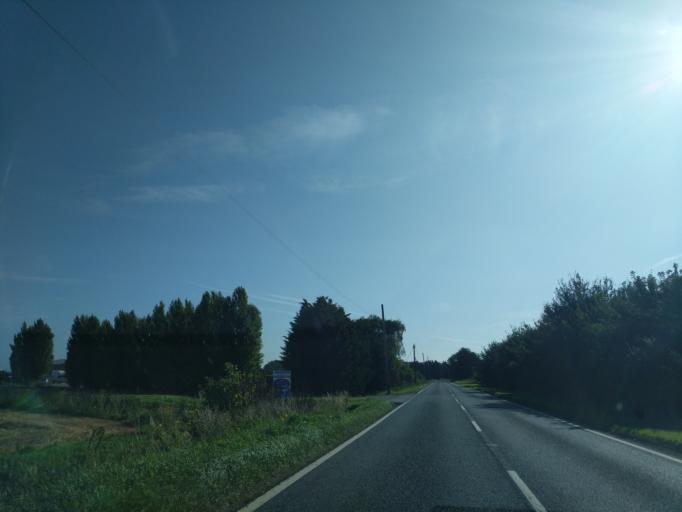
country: GB
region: England
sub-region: Lincolnshire
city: Bourne
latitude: 52.7717
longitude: -0.3507
